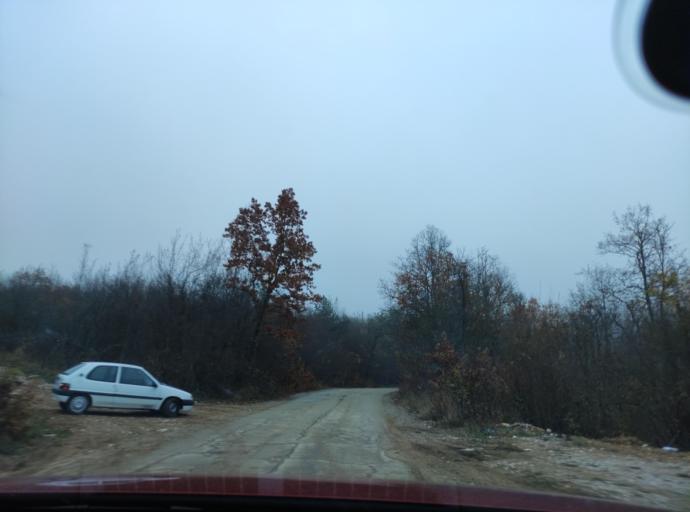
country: BG
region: Lovech
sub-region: Obshtina Yablanitsa
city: Yablanitsa
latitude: 43.1100
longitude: 24.0688
